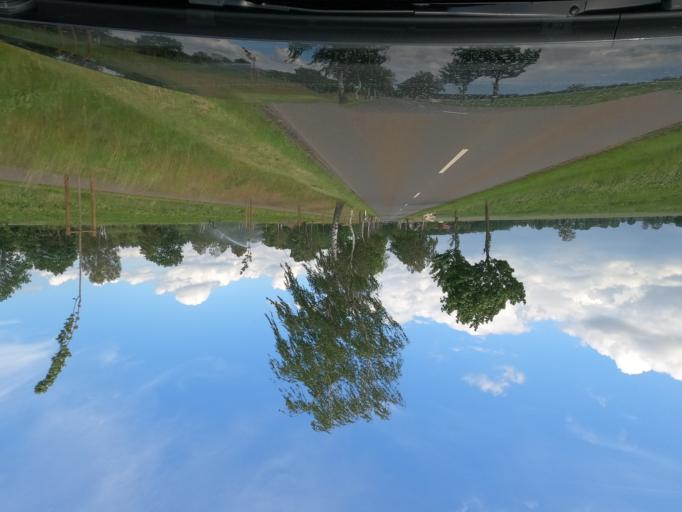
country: DE
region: Lower Saxony
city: Lindwedel
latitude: 52.6282
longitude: 9.6473
